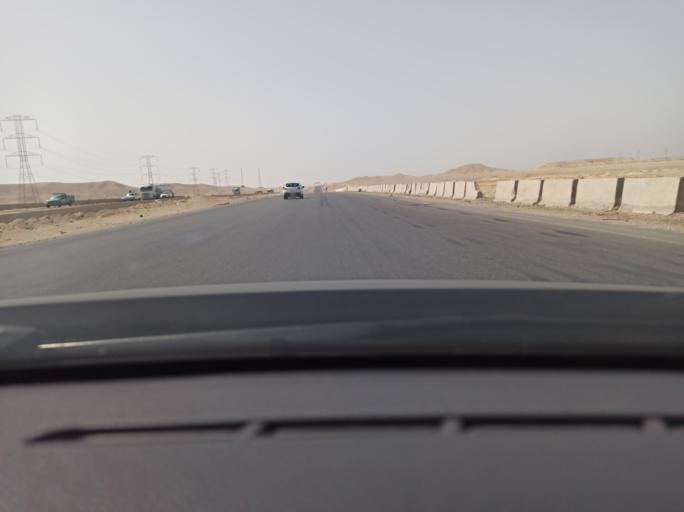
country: EG
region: Al Jizah
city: As Saff
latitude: 29.5512
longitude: 31.3966
